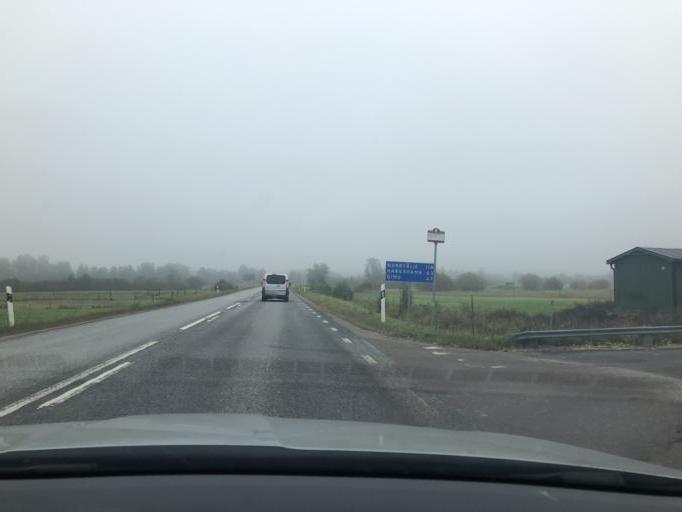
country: SE
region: Uppsala
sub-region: Tierps Kommun
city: Tierp
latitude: 60.3312
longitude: 17.5113
